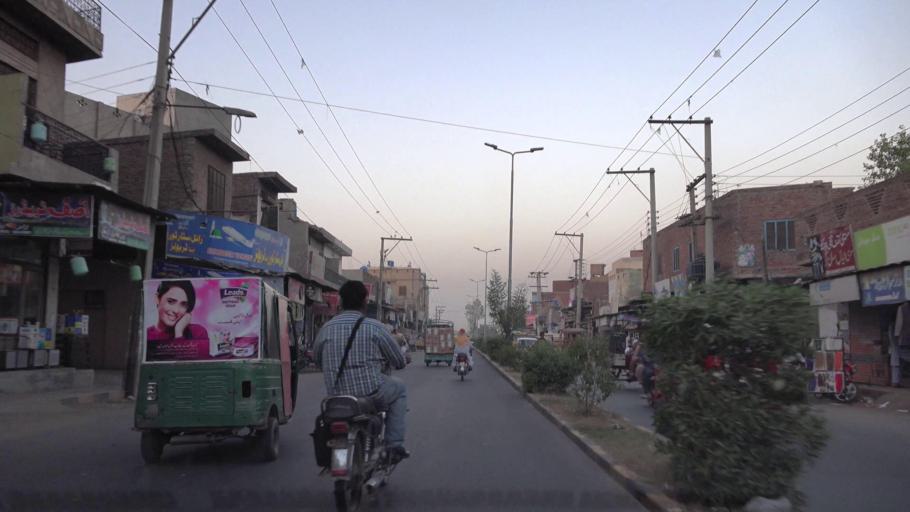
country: PK
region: Punjab
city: Faisalabad
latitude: 31.4455
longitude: 73.0960
